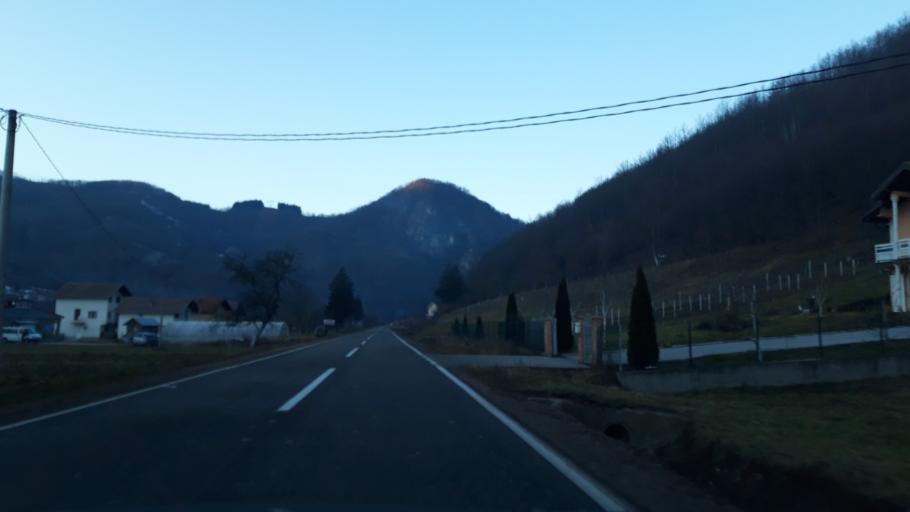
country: BA
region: Republika Srpska
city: Milici
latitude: 44.2588
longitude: 19.1065
